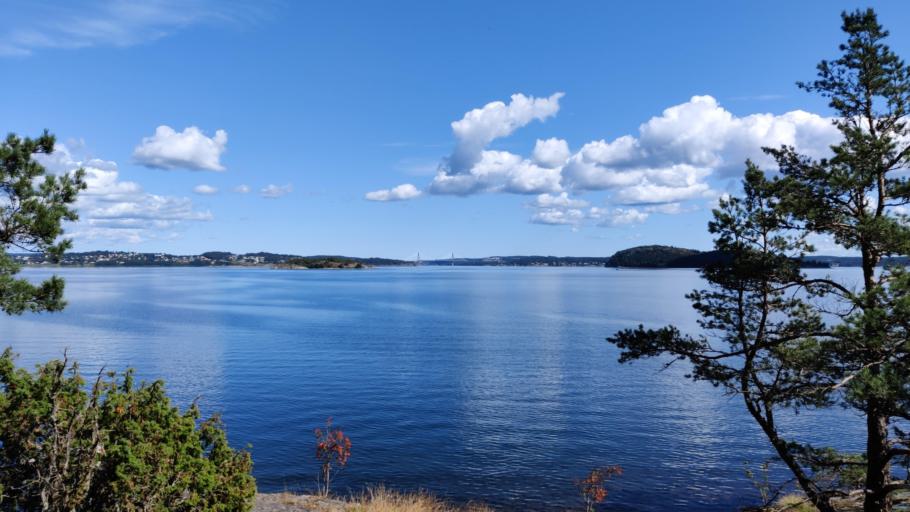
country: SE
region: Vaestra Goetaland
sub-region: Orust
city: Henan
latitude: 58.3090
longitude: 11.7302
